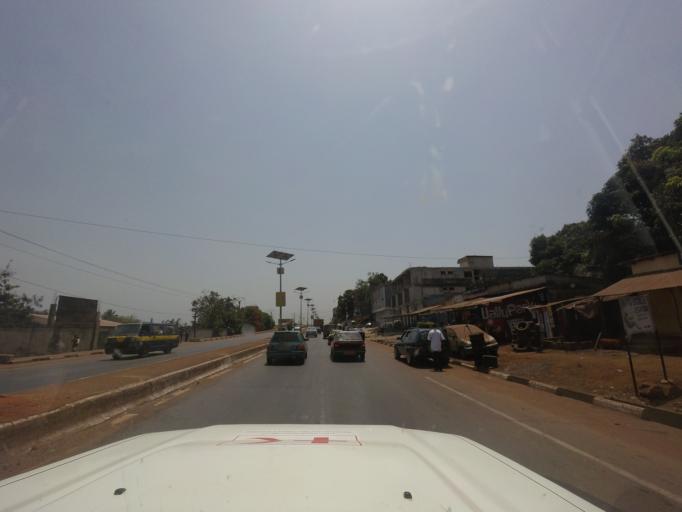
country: GN
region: Conakry
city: Conakry
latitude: 9.6290
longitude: -13.5760
